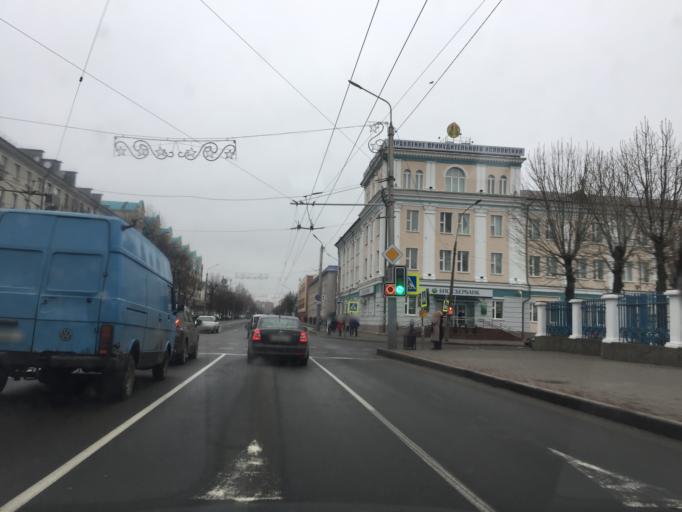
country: BY
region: Mogilev
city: Mahilyow
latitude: 53.9112
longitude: 30.3411
